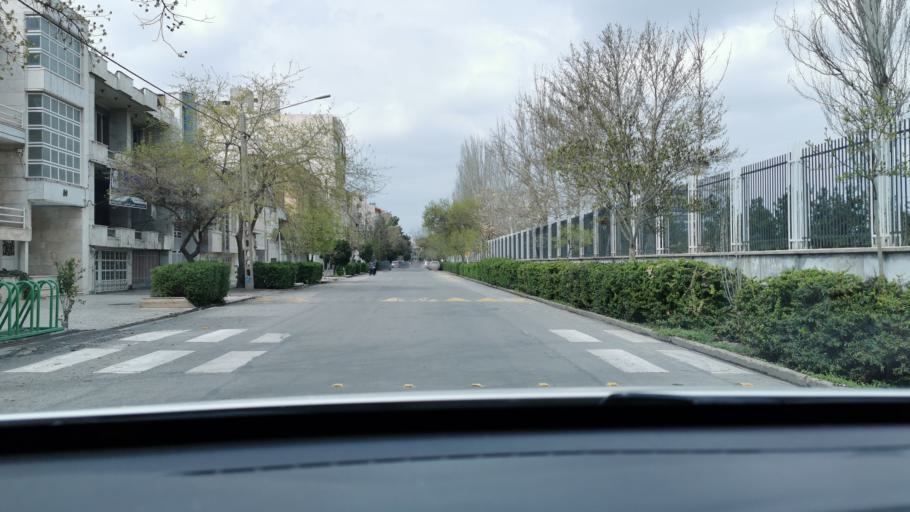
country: IR
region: Razavi Khorasan
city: Mashhad
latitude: 36.2860
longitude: 59.5789
